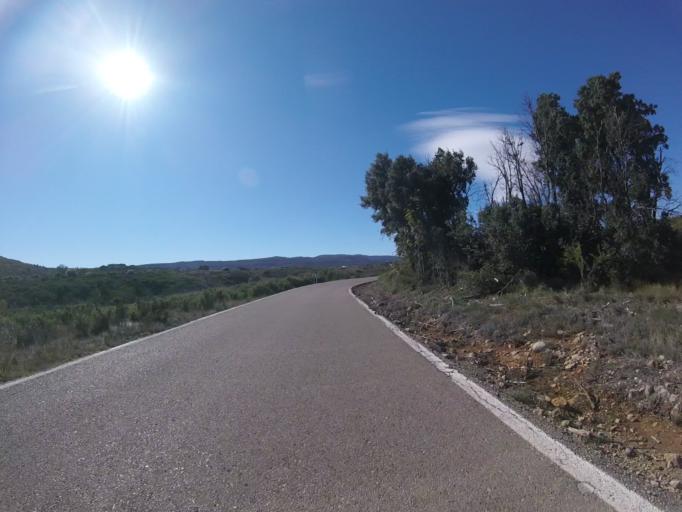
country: ES
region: Valencia
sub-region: Provincia de Castello
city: Albocasser
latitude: 40.3776
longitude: 0.0213
